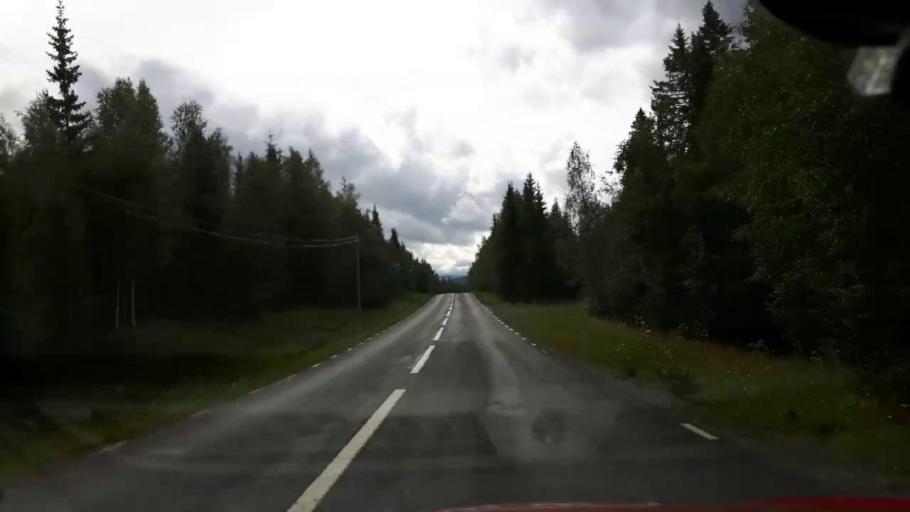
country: NO
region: Nord-Trondelag
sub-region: Lierne
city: Sandvika
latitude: 64.5221
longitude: 14.1637
